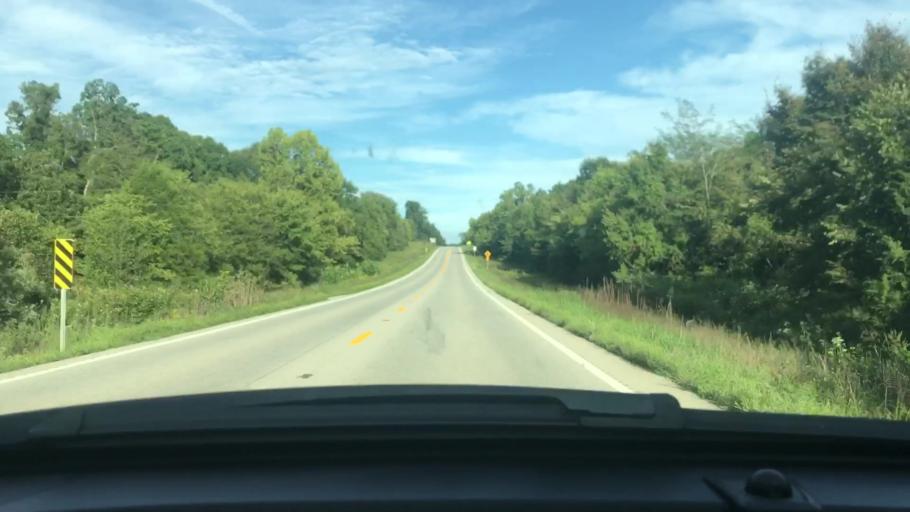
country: US
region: Arkansas
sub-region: Sharp County
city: Cherokee Village
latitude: 36.2745
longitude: -91.3463
